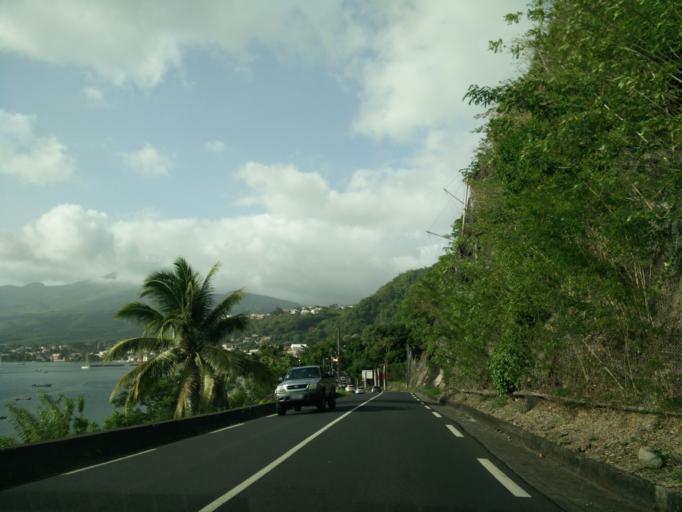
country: MQ
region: Martinique
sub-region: Martinique
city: Saint-Pierre
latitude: 14.7348
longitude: -61.1777
